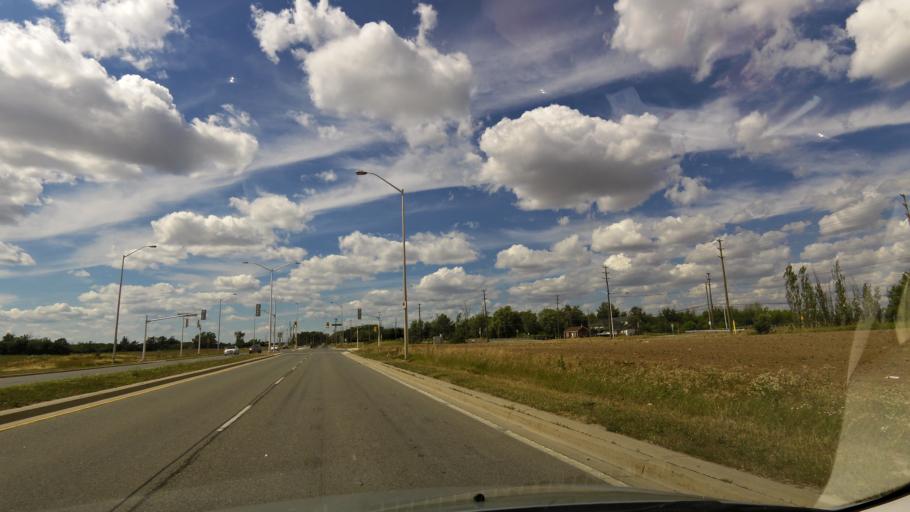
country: CA
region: Ontario
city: Burlington
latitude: 43.4371
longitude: -79.7801
